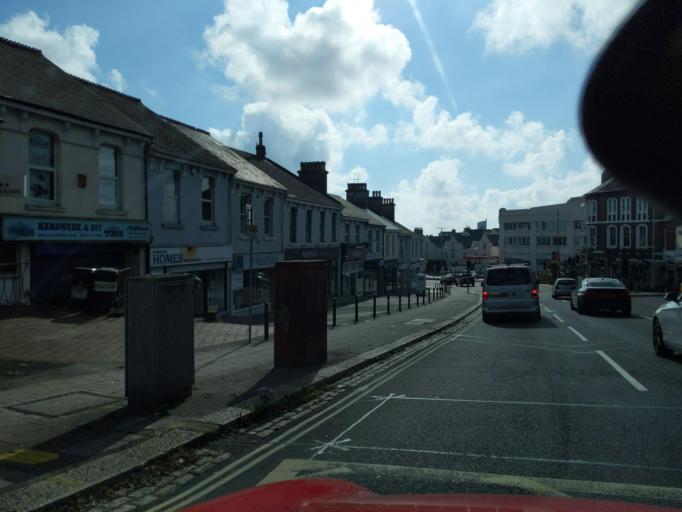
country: GB
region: England
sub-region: Plymouth
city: Plymouth
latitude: 50.3847
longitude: -4.1339
